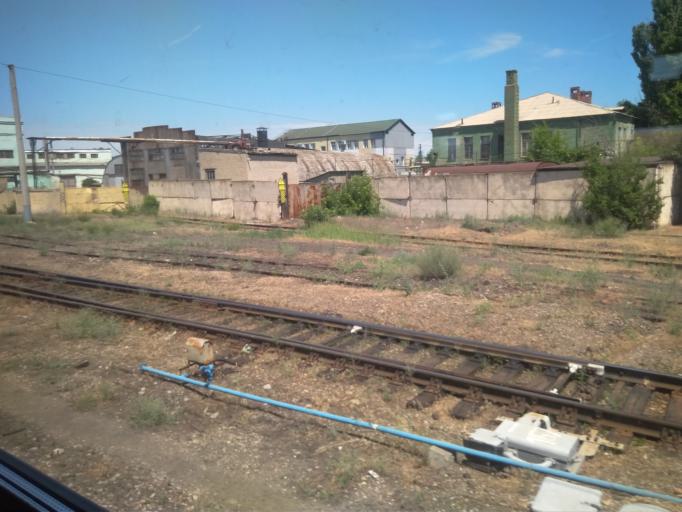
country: RU
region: Volgograd
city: Volgograd
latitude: 48.5236
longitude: 44.5041
